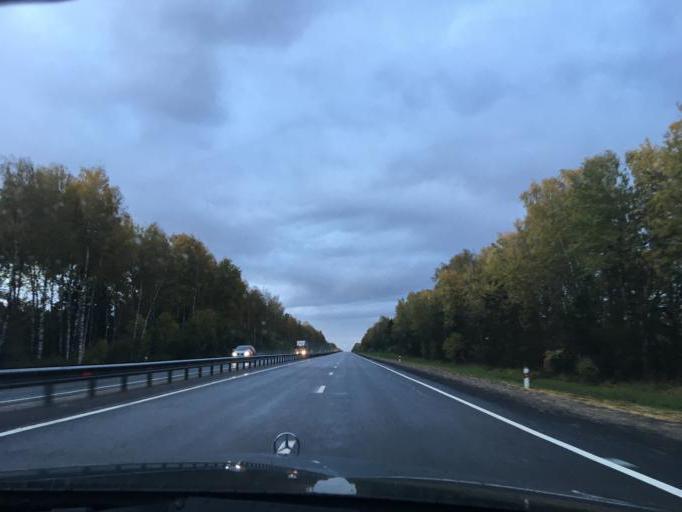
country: RU
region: Smolensk
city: Safonovo
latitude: 55.1223
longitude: 33.0928
